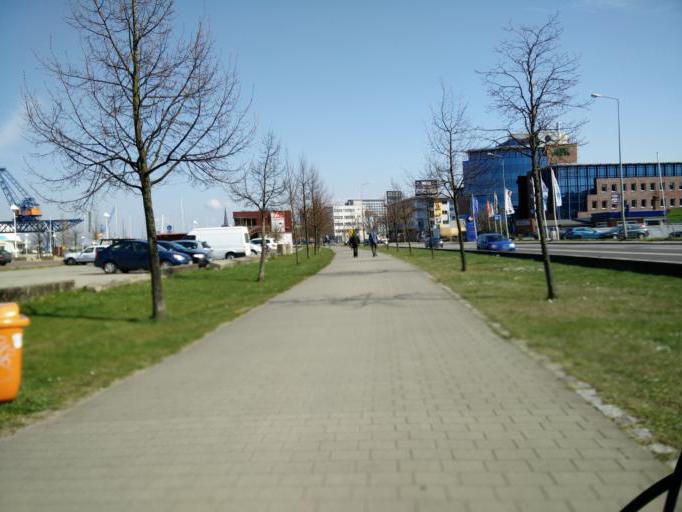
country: DE
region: Mecklenburg-Vorpommern
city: Rostock
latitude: 54.0927
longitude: 12.1203
